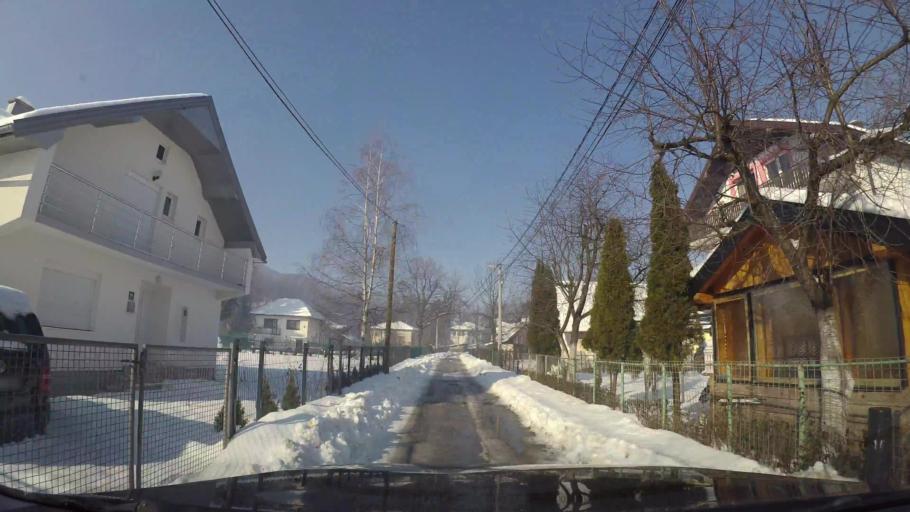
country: BA
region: Federation of Bosnia and Herzegovina
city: Gracanica
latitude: 43.8036
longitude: 18.2997
